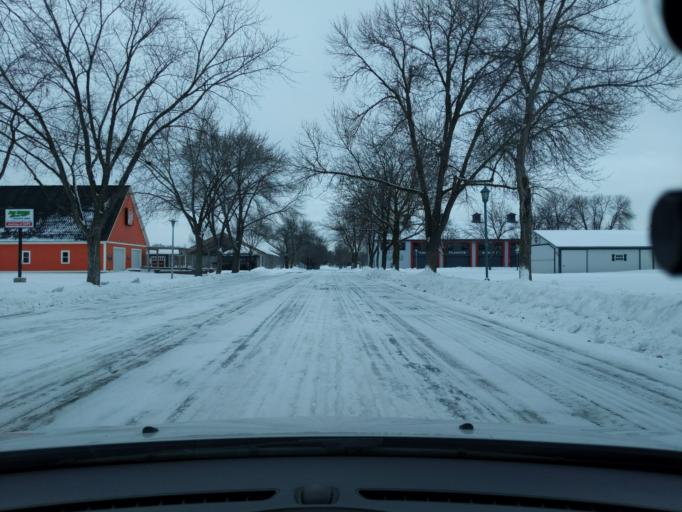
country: US
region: Minnesota
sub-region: Ramsey County
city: Falcon Heights
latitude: 44.9863
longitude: -93.1705
